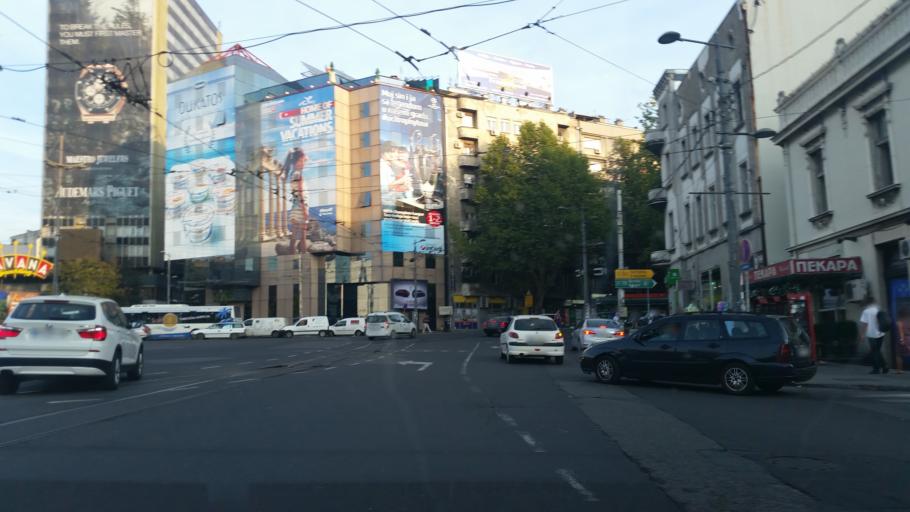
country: RS
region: Central Serbia
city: Belgrade
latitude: 44.8024
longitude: 20.4656
